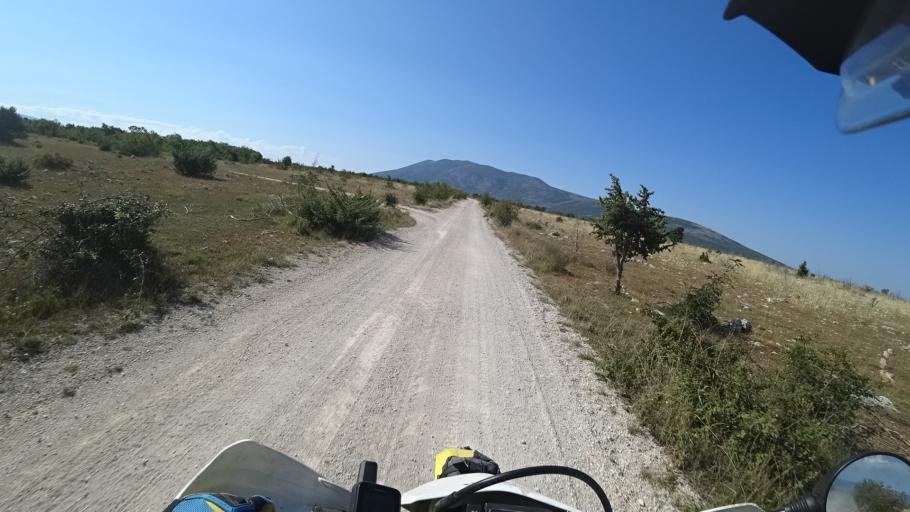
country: HR
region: Sibensko-Kniniska
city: Knin
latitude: 43.9882
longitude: 16.1916
